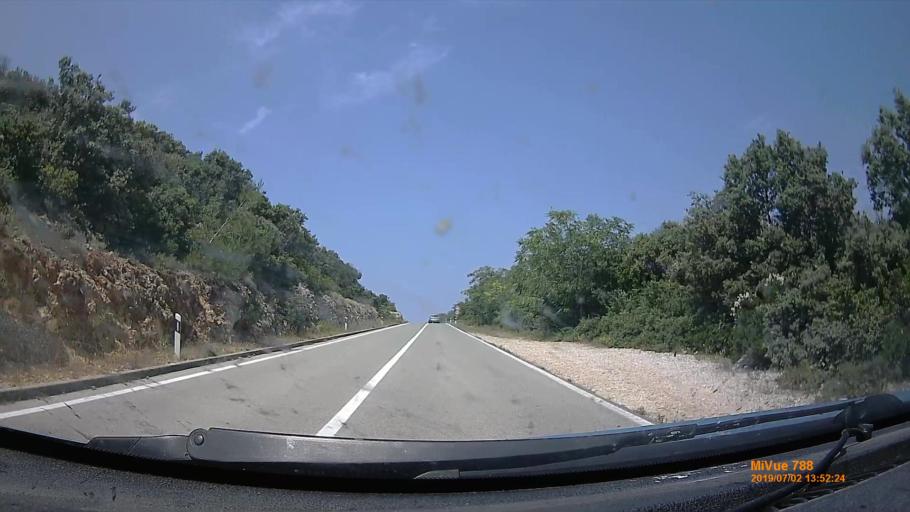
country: HR
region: Primorsko-Goranska
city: Mali Losinj
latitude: 44.6137
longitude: 14.3970
